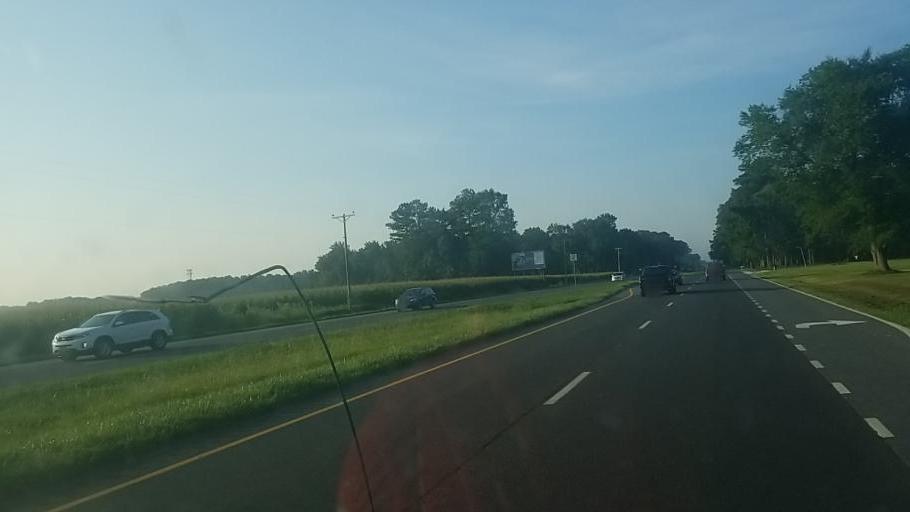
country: US
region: Delaware
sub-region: Sussex County
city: Selbyville
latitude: 38.4759
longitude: -75.2352
